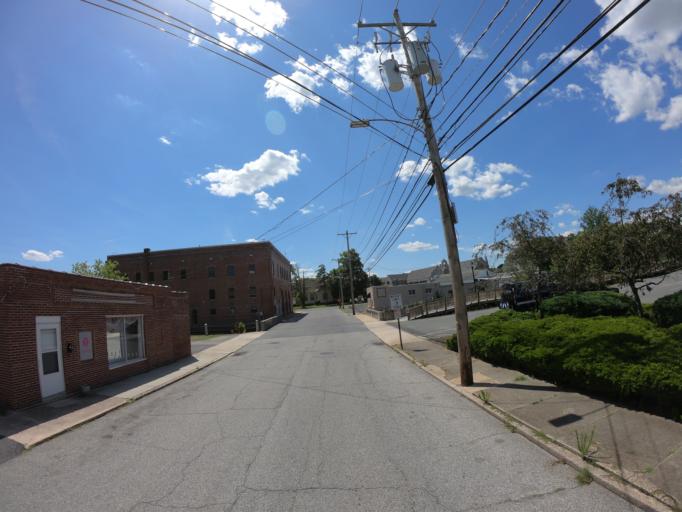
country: US
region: Delaware
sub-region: Sussex County
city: Milford
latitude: 38.9129
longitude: -75.4295
